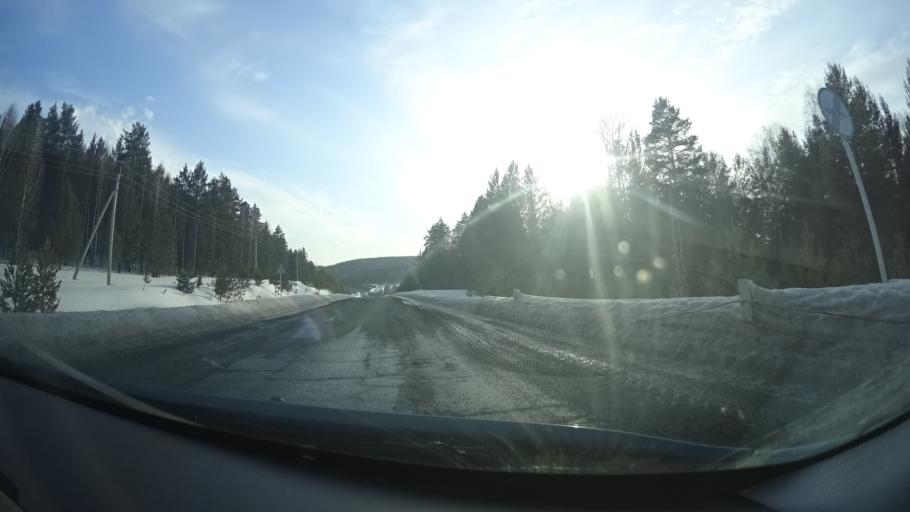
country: RU
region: Bashkortostan
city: Lomovka
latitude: 53.6708
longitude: 58.2267
